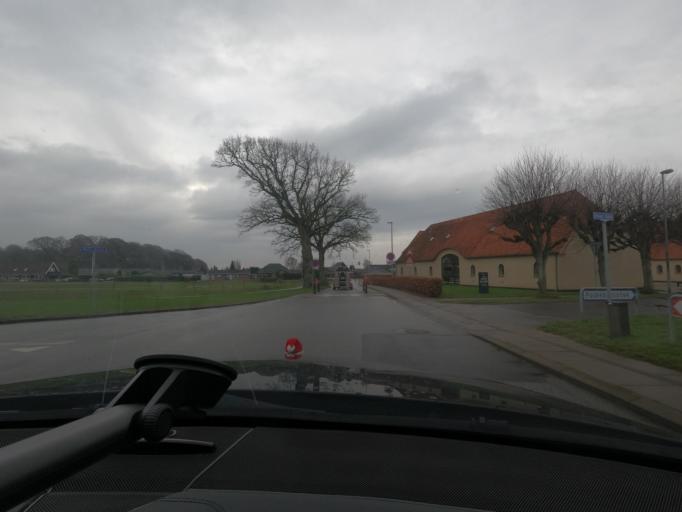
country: DK
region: South Denmark
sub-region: Sonderborg Kommune
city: Horuphav
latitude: 54.9146
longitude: 9.8945
